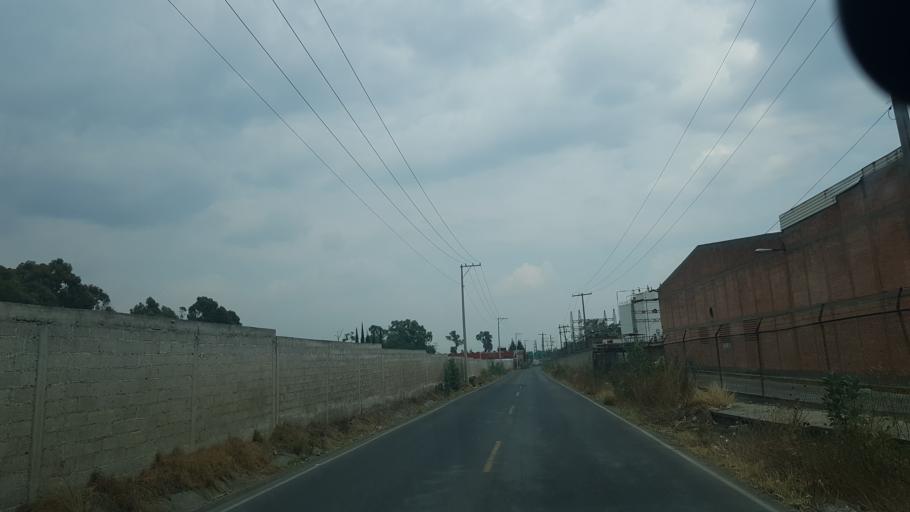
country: MX
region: Puebla
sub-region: Huejotzingo
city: San Mateo Capultitlan
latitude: 19.2024
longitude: -98.4237
